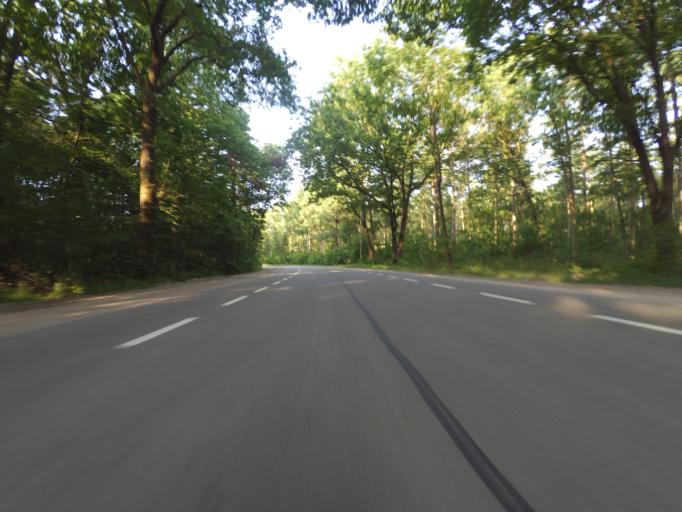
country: NL
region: Gelderland
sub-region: Gemeente Apeldoorn
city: Beekbergen
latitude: 52.1271
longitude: 5.9555
